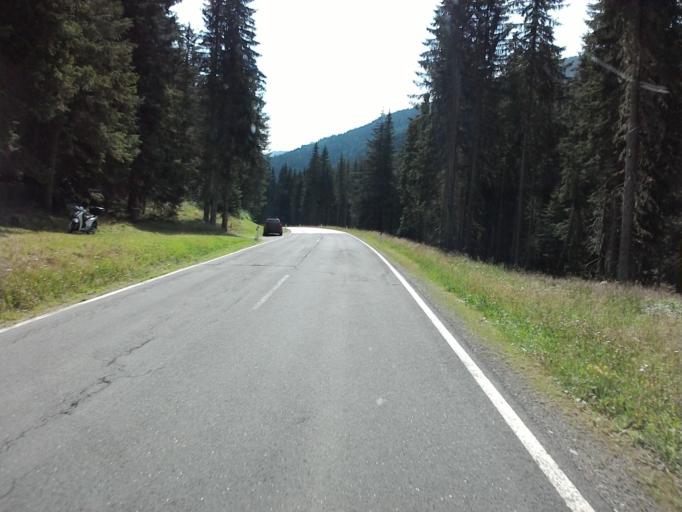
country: AT
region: Tyrol
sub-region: Politischer Bezirk Lienz
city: Obertilliach
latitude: 46.7117
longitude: 12.5795
